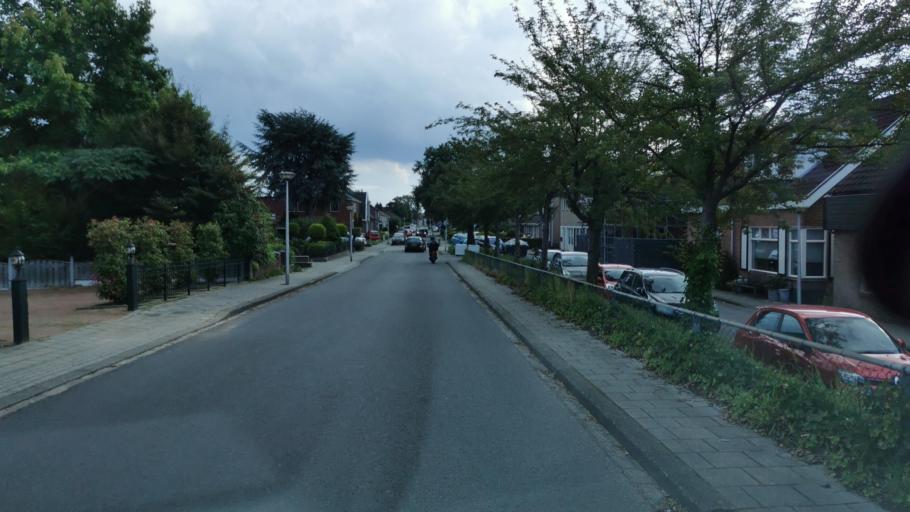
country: NL
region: Overijssel
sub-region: Gemeente Losser
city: Losser
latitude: 52.2194
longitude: 6.9650
